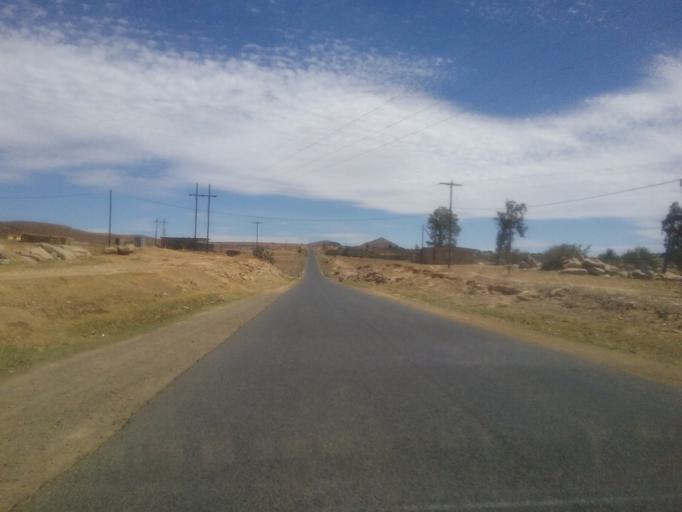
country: LS
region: Mafeteng
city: Mafeteng
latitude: -29.9383
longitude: 27.2647
